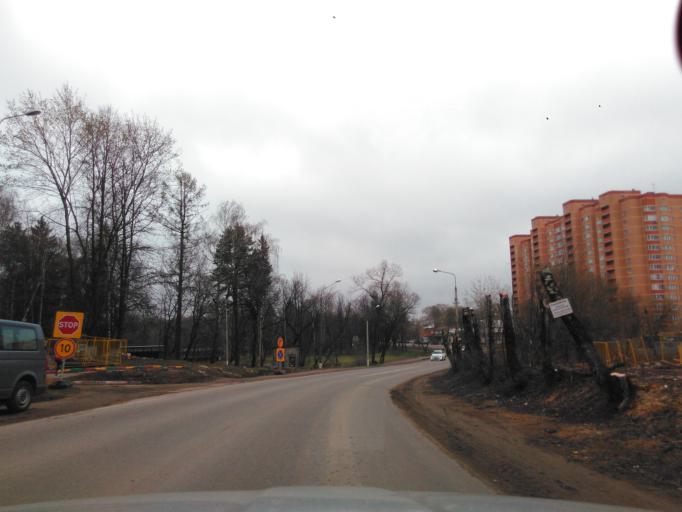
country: RU
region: Moskovskaya
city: Nakhabino
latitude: 55.8385
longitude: 37.1603
